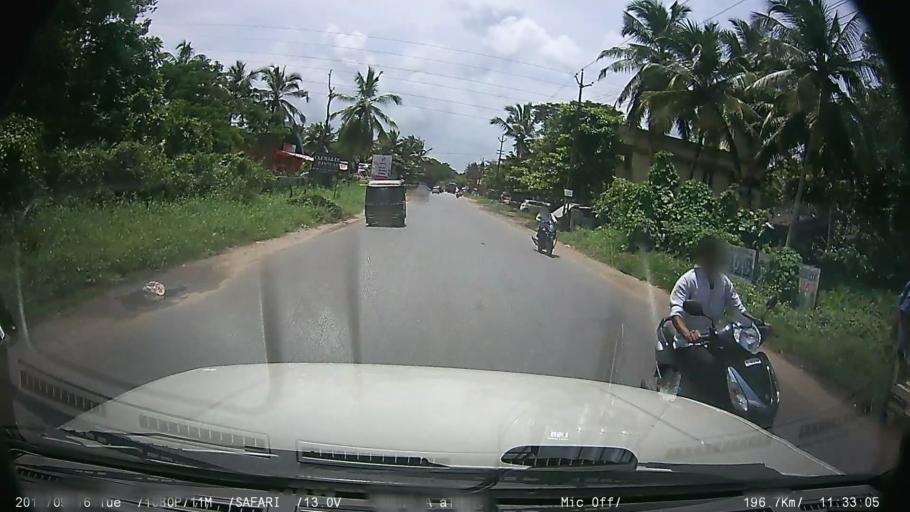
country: IN
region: Kerala
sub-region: Kottayam
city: Changanacheri
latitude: 9.4697
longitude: 76.5294
